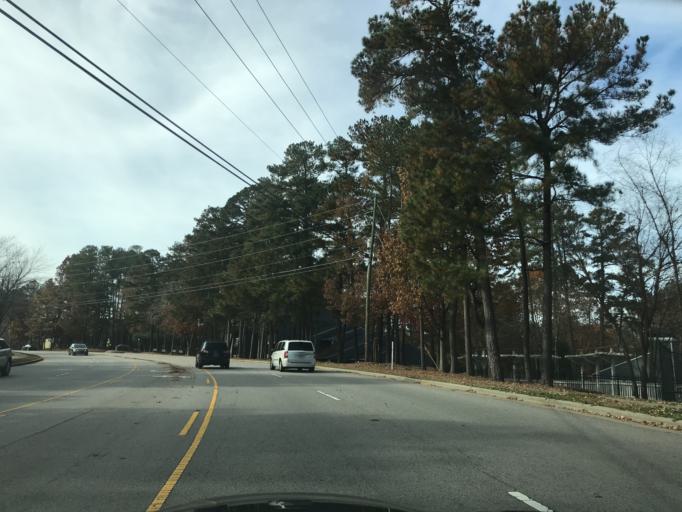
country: US
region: North Carolina
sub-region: Wake County
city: West Raleigh
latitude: 35.8579
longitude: -78.6669
